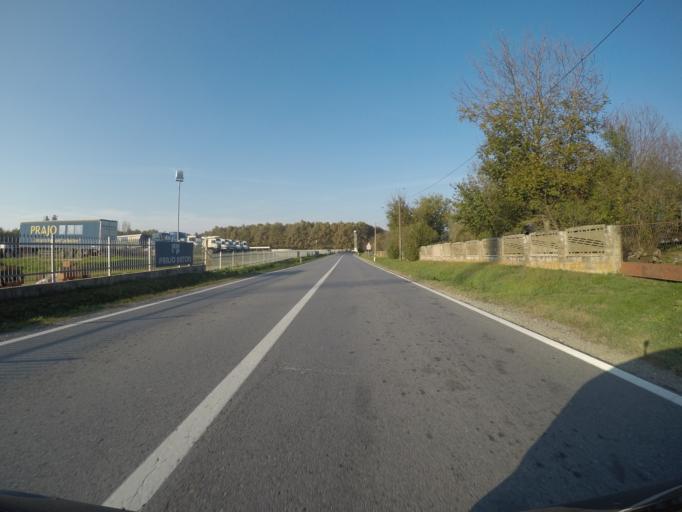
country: HR
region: Virovitick-Podravska
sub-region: Grad Virovitica
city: Virovitica
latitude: 45.8766
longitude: 17.4050
